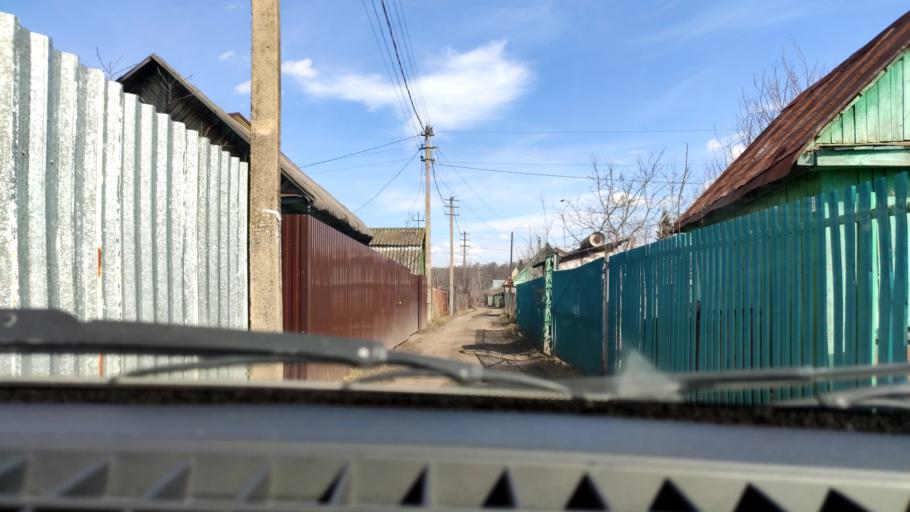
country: RU
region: Bashkortostan
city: Avdon
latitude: 54.6779
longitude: 55.8186
